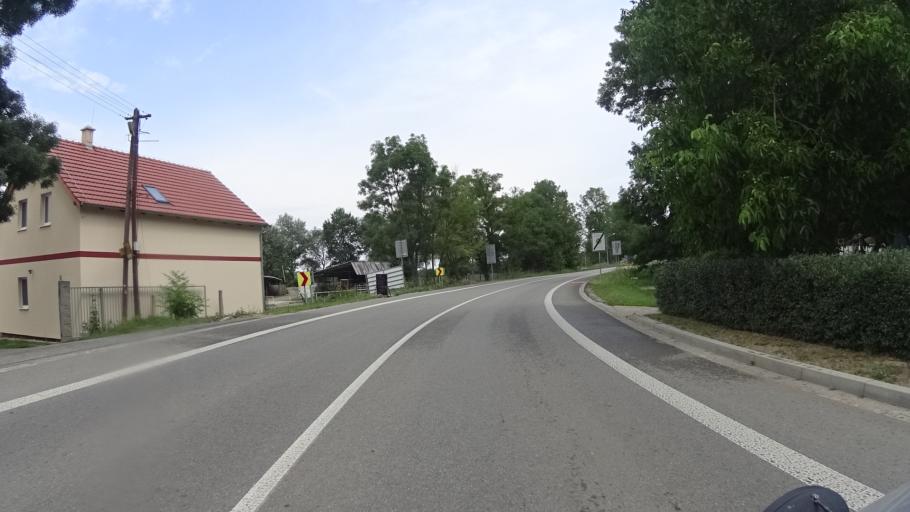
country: CZ
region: South Moravian
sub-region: Okres Breclav
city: Lednice
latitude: 48.8067
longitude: 16.8041
